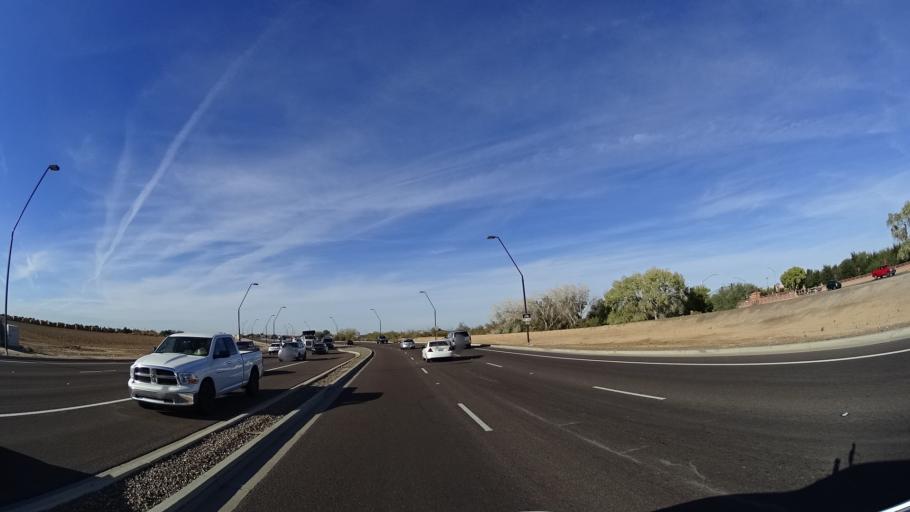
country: US
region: Arizona
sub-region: Maricopa County
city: Queen Creek
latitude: 33.2398
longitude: -111.6350
